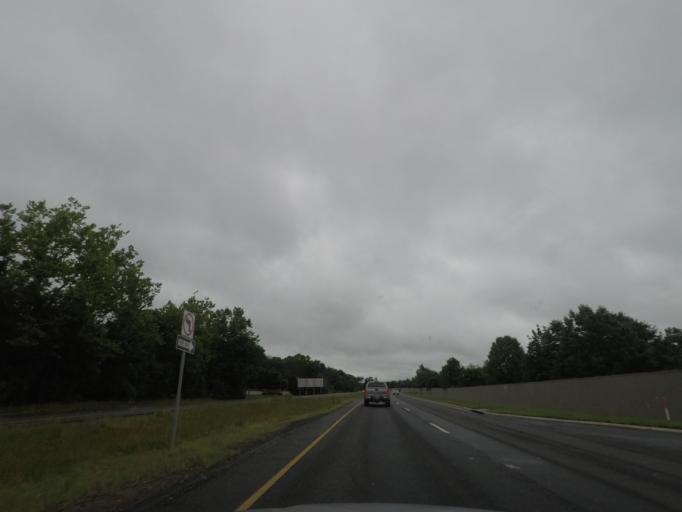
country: US
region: Virginia
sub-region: Prince William County
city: Haymarket
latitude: 38.8300
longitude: -77.6331
